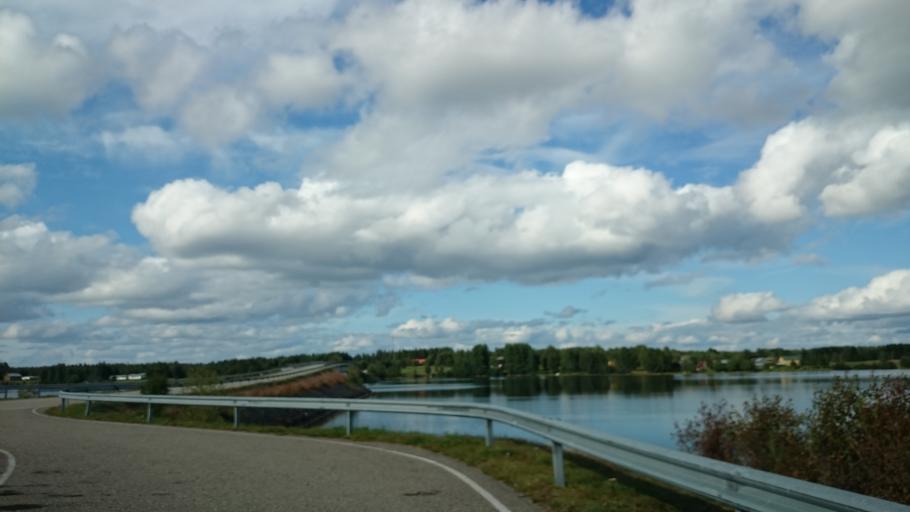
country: FI
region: Kainuu
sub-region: Kehys-Kainuu
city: Suomussalmi
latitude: 64.7391
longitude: 29.4395
